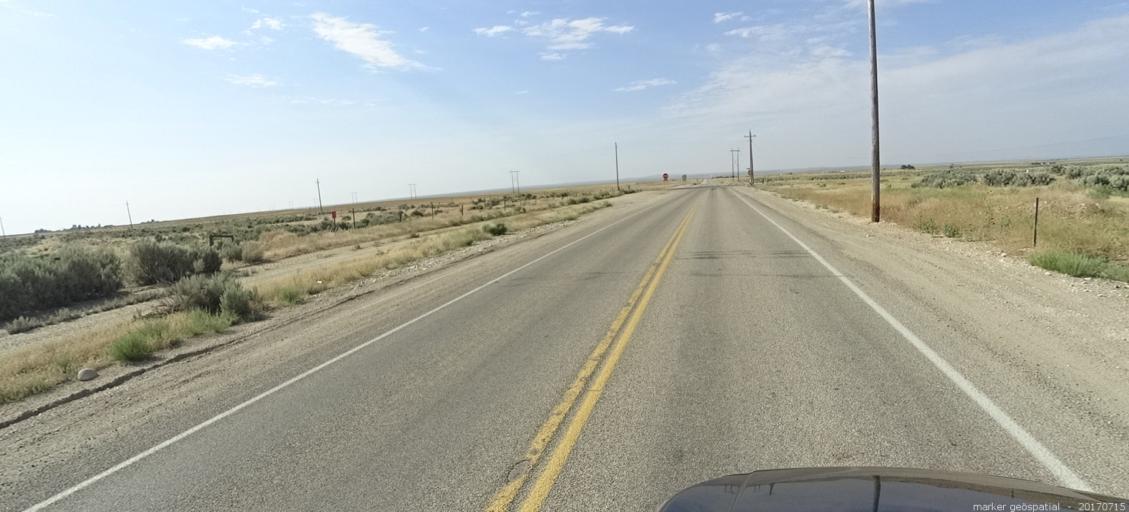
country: US
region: Idaho
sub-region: Ada County
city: Boise
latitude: 43.4602
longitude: -116.2344
